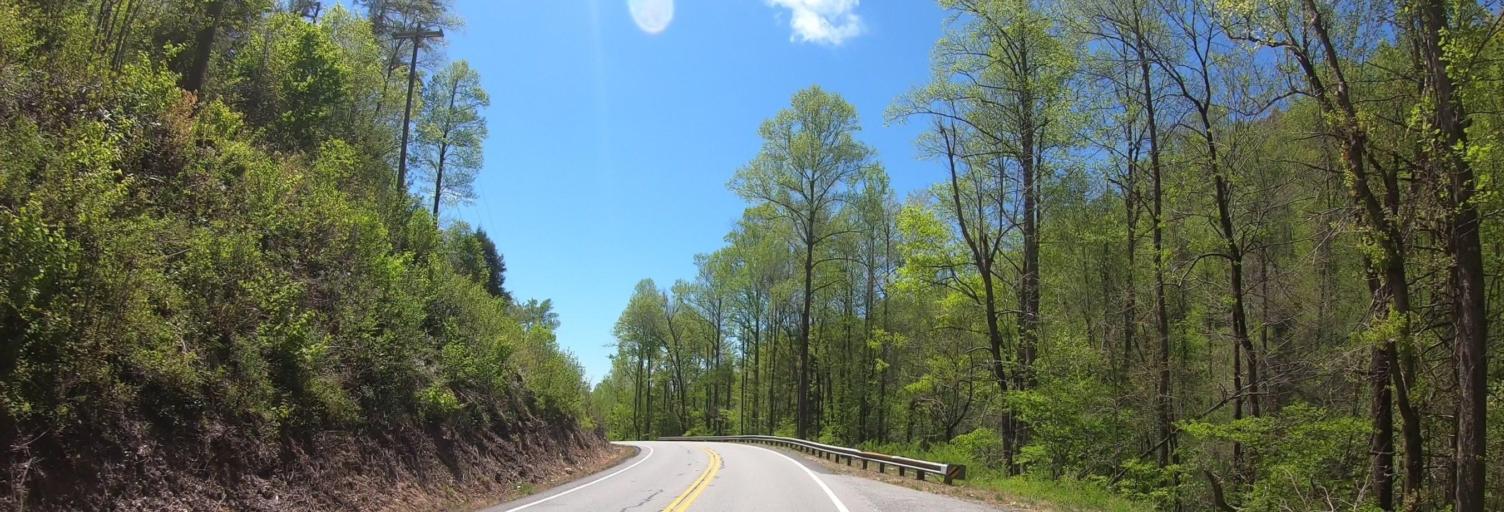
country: US
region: Georgia
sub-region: White County
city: Cleveland
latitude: 34.7553
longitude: -83.7499
